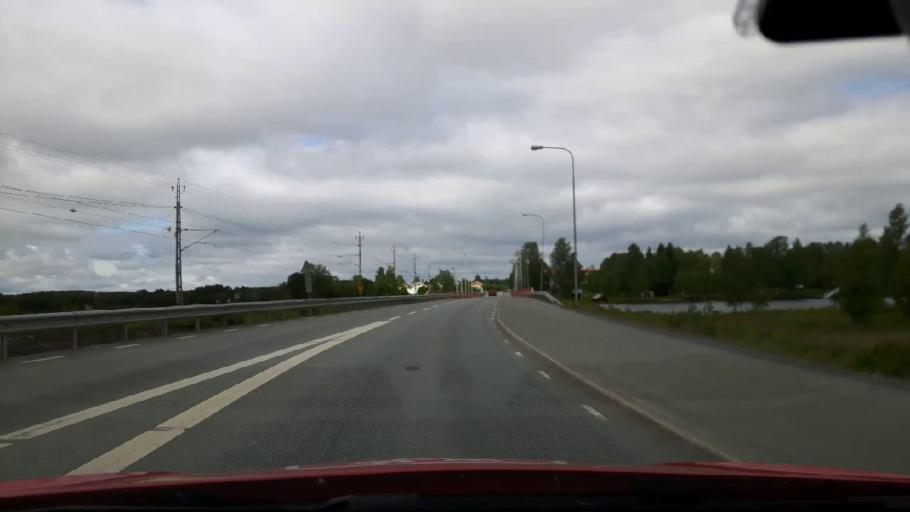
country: SE
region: Jaemtland
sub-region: Krokoms Kommun
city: Krokom
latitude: 63.3219
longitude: 14.4549
